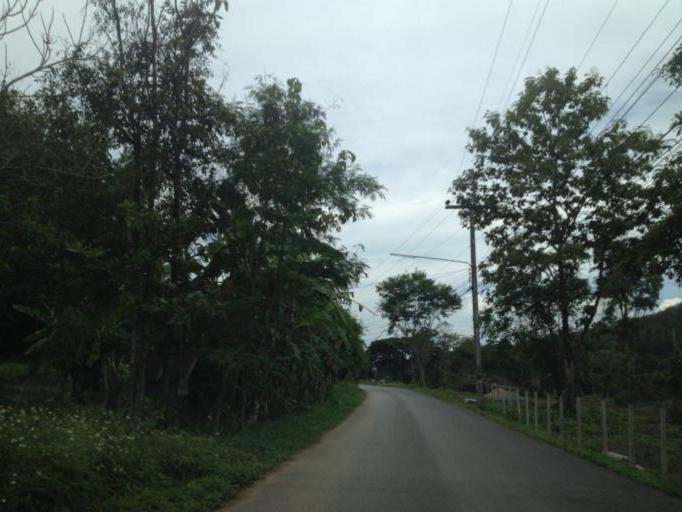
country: TH
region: Chiang Mai
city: Hang Dong
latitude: 18.6953
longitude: 98.8669
